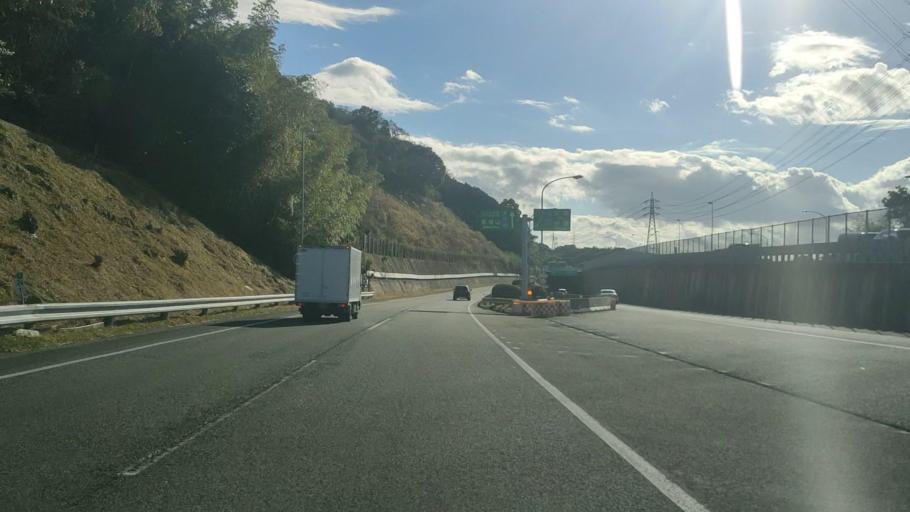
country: JP
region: Fukuoka
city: Kitakyushu
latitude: 33.8462
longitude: 130.7666
